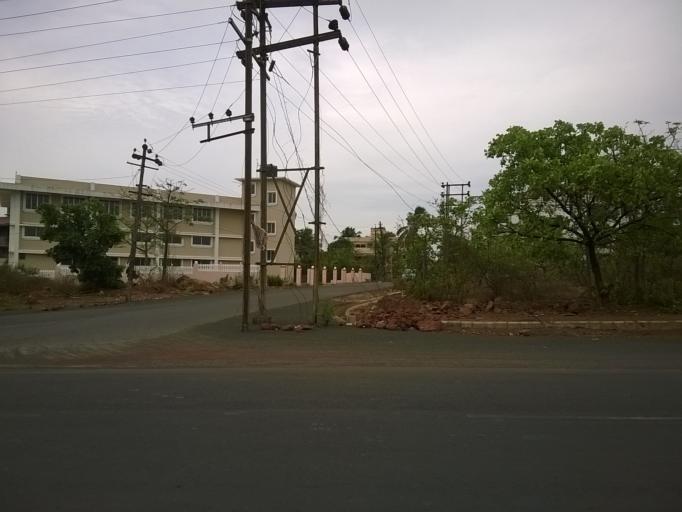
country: IN
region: Goa
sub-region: North Goa
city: Serula
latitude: 15.5384
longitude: 73.8181
